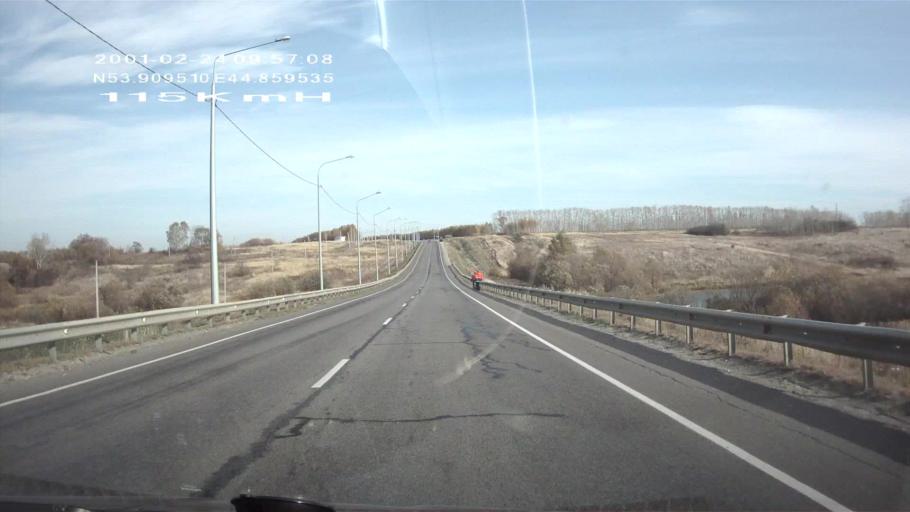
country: RU
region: Penza
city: Issa
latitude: 53.9094
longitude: 44.8598
